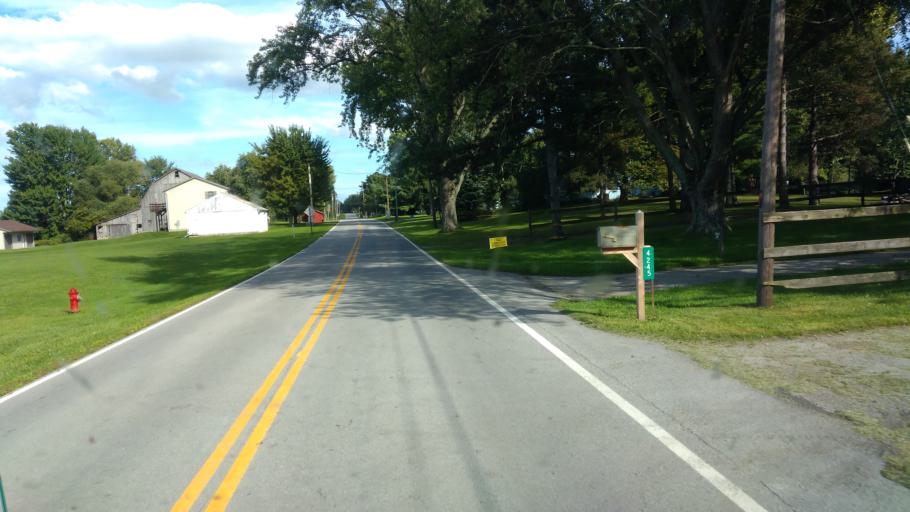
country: US
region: Ohio
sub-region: Sandusky County
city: Clyde
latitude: 41.2862
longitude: -82.9691
